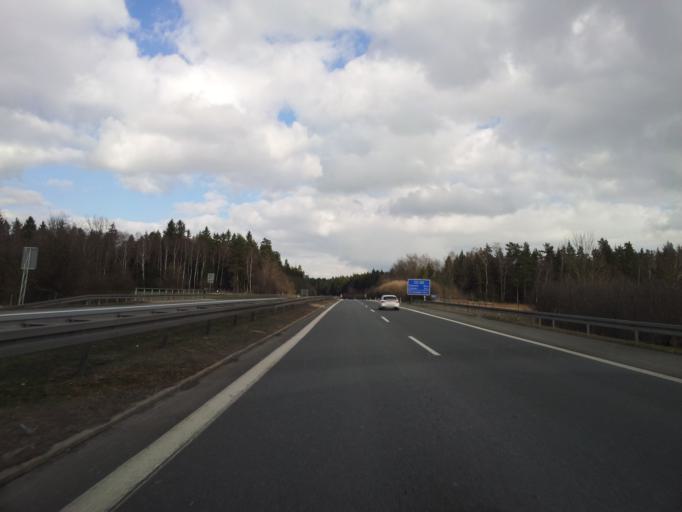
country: DE
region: Saxony
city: Waldkirchen
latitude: 50.5980
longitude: 12.3509
